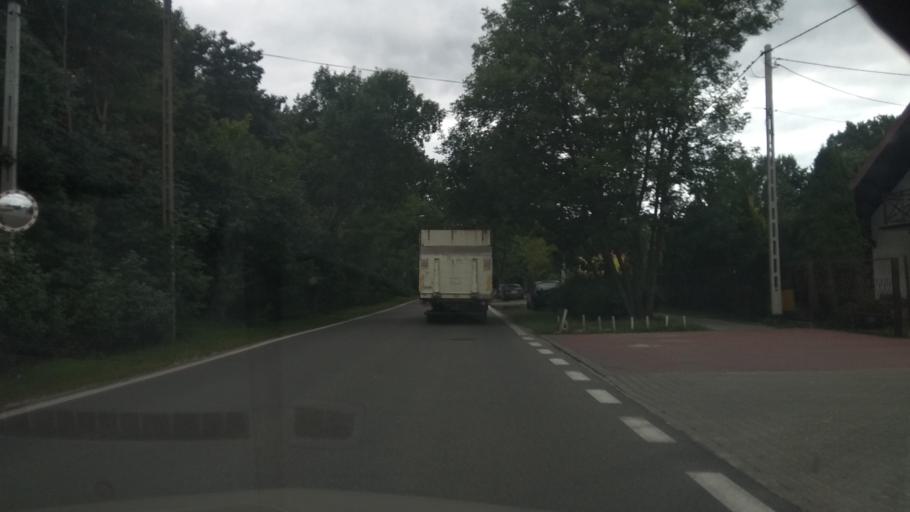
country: PL
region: Masovian Voivodeship
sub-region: Warszawa
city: Wawer
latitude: 52.2142
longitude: 21.1409
